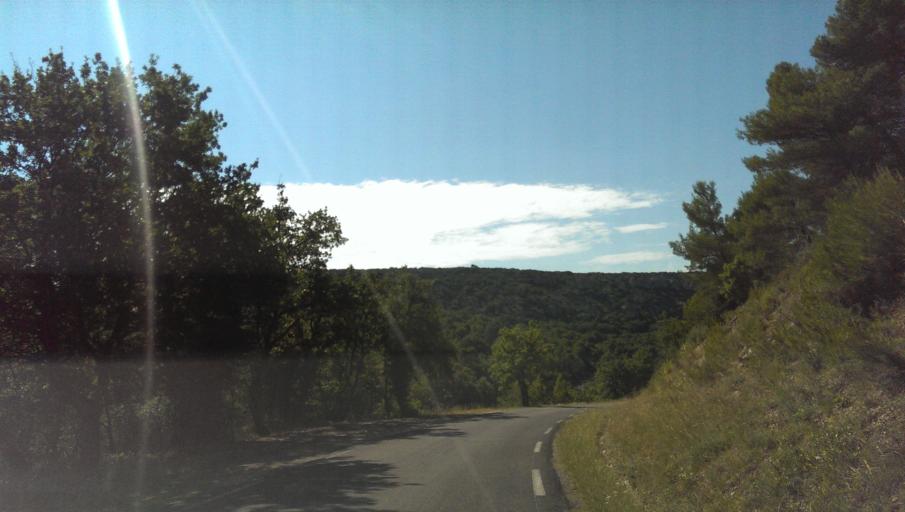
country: FR
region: Provence-Alpes-Cote d'Azur
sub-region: Departement du Vaucluse
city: Gordes
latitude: 43.9361
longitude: 5.1880
